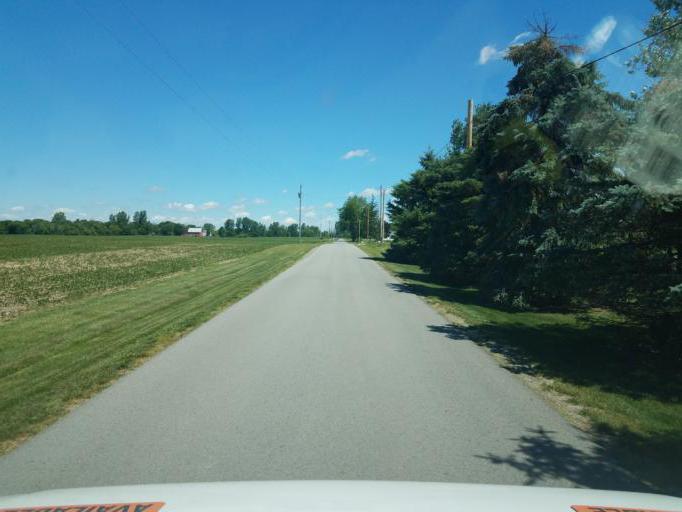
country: US
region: Ohio
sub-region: Morrow County
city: Cardington
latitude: 40.6104
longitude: -82.9380
